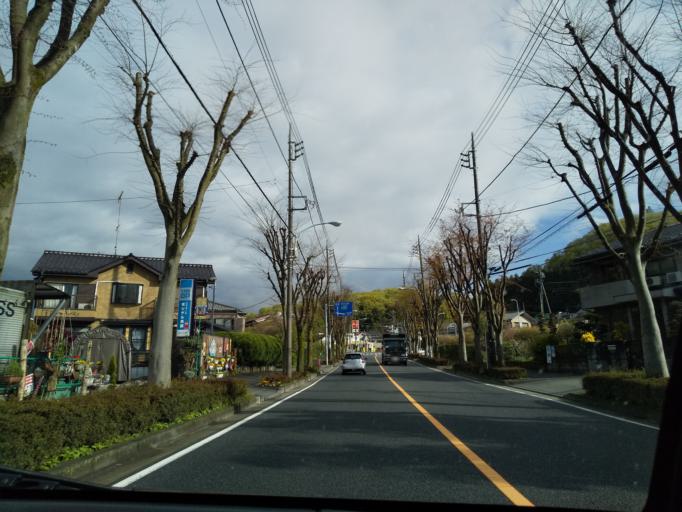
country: JP
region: Tokyo
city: Itsukaichi
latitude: 35.6882
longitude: 139.2506
